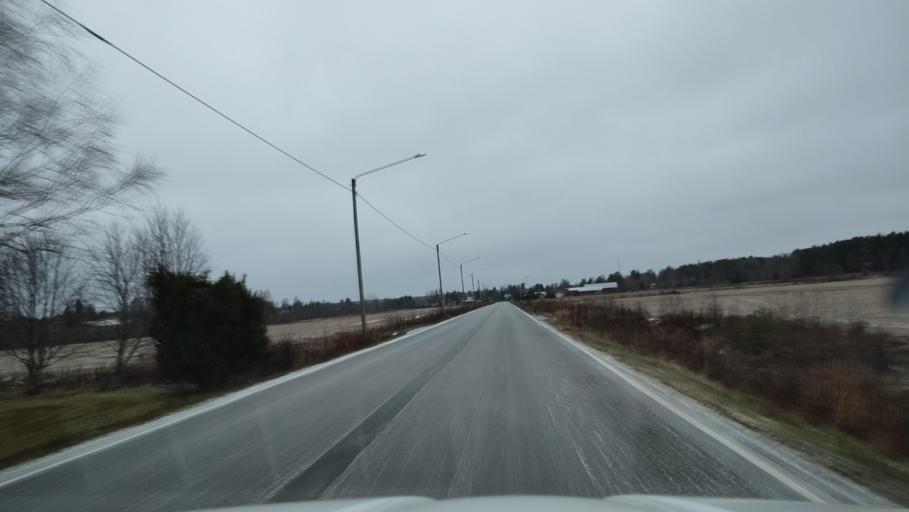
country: FI
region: Southern Ostrobothnia
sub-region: Suupohja
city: Karijoki
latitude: 62.2379
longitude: 21.6572
